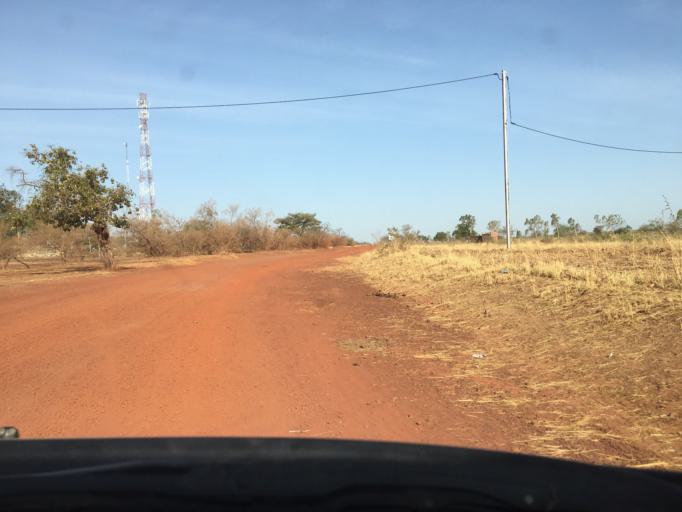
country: BF
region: Plateau-Central
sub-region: Province du Kourweogo
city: Bousse
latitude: 12.5578
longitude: -1.8970
